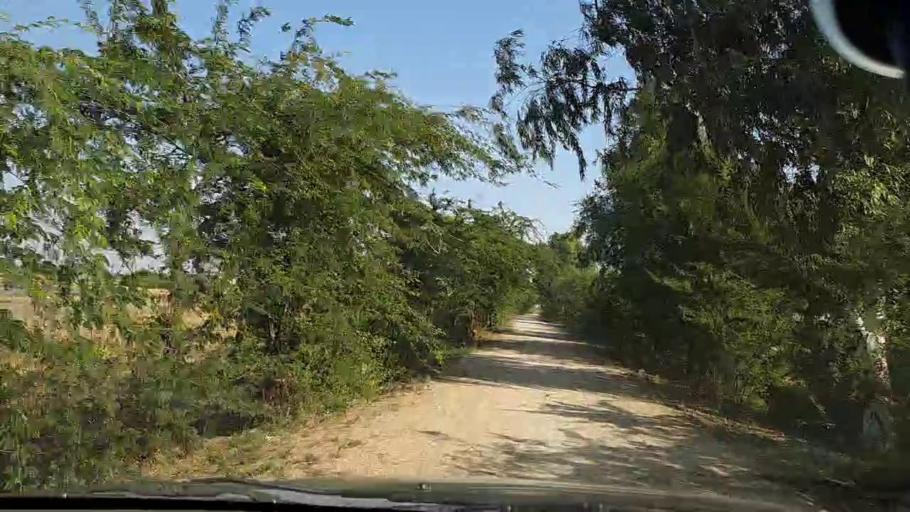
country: PK
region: Sindh
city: Mirpur Batoro
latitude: 24.6291
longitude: 68.2674
